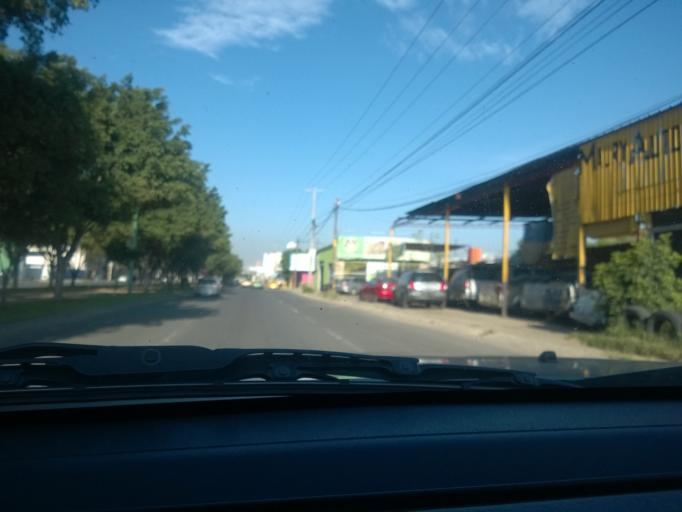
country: MX
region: Guanajuato
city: Leon
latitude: 21.1276
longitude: -101.6418
